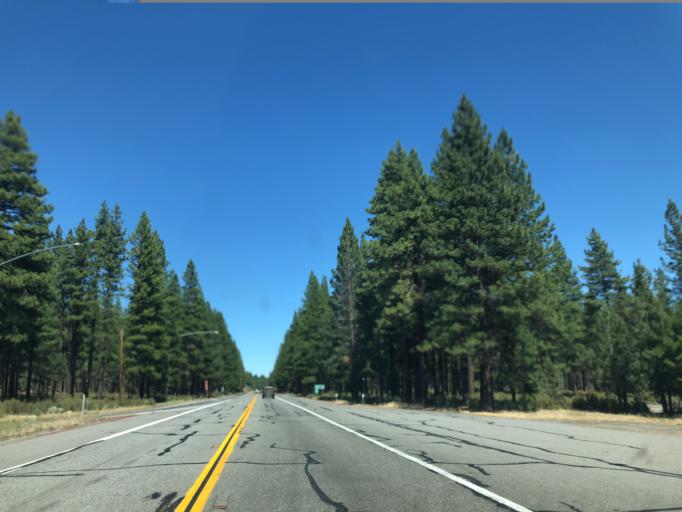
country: US
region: California
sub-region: Lassen County
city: Susanville
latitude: 40.4112
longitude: -120.7554
